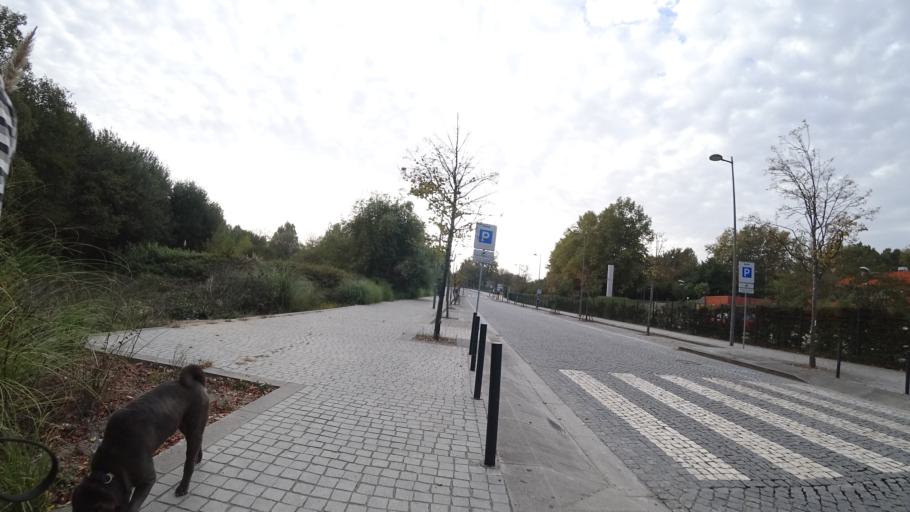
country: PT
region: Porto
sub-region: Matosinhos
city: Sao Mamede de Infesta
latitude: 41.1768
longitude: -8.6018
